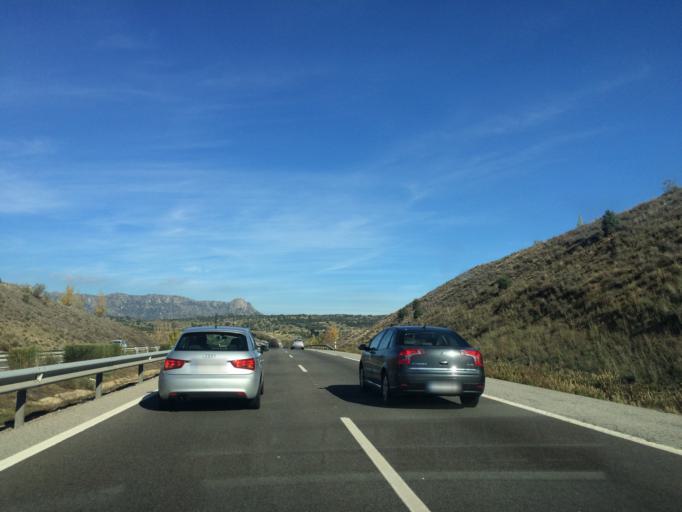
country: ES
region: Madrid
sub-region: Provincia de Madrid
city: Cabanillas de la Sierra
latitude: 40.8194
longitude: -3.6154
